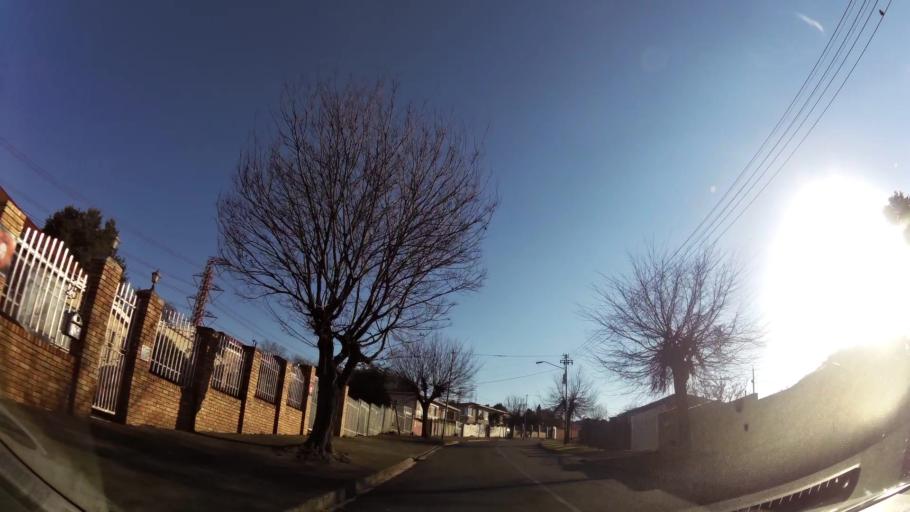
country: ZA
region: Gauteng
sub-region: Ekurhuleni Metropolitan Municipality
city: Germiston
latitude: -26.1913
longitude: 28.1469
